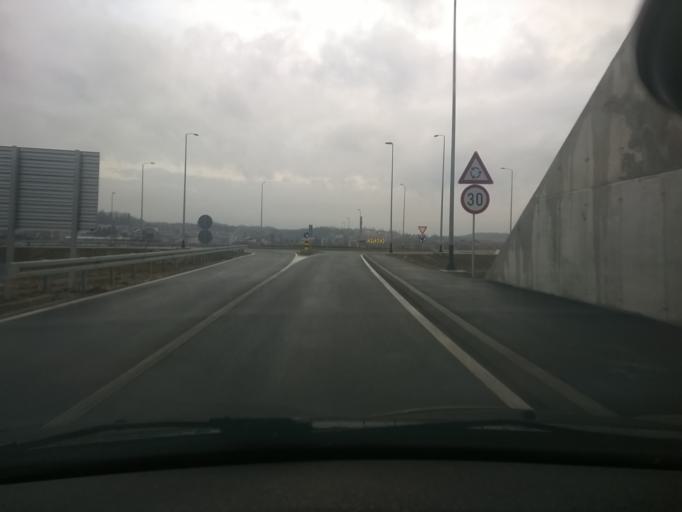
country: HR
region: Krapinsko-Zagorska
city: Bedekovcina
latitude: 46.0327
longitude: 15.9940
